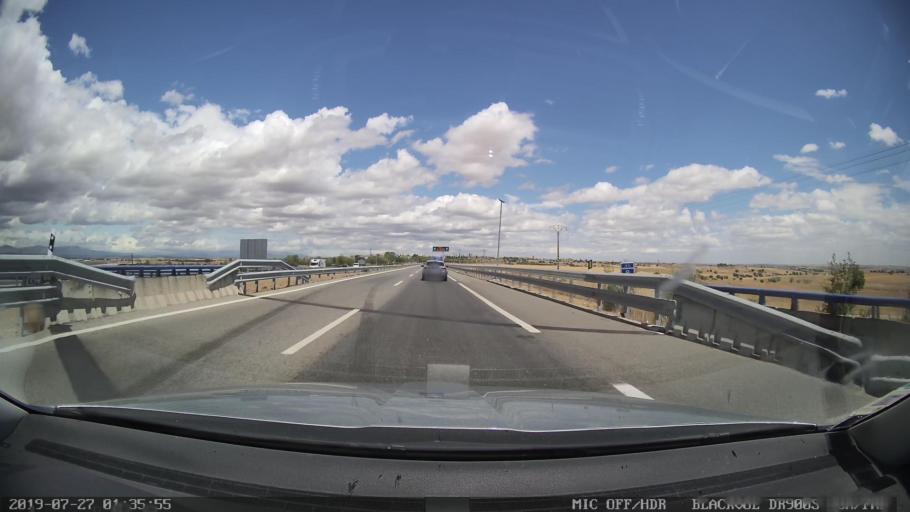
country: ES
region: Madrid
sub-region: Provincia de Madrid
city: Navalcarnero
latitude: 40.2725
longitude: -4.0328
